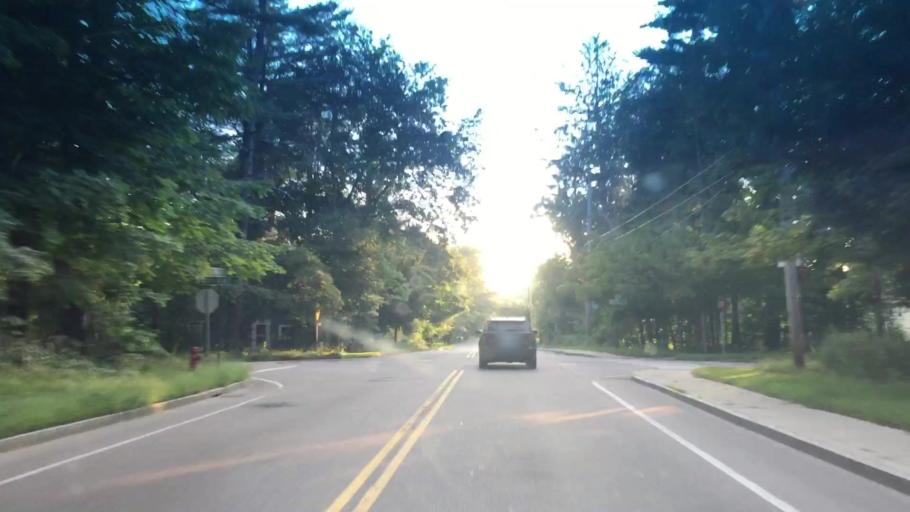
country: US
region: Massachusetts
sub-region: Norfolk County
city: Medfield
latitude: 42.1824
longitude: -71.3190
